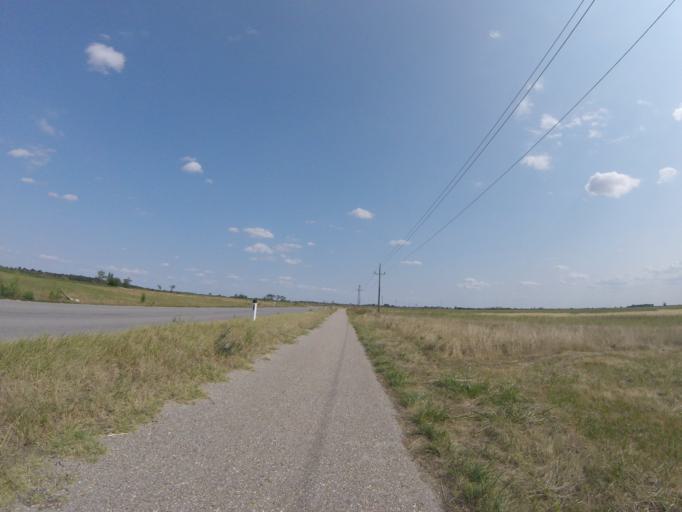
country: AT
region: Burgenland
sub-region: Politischer Bezirk Neusiedl am See
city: Apetlon
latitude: 47.7269
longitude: 16.8598
